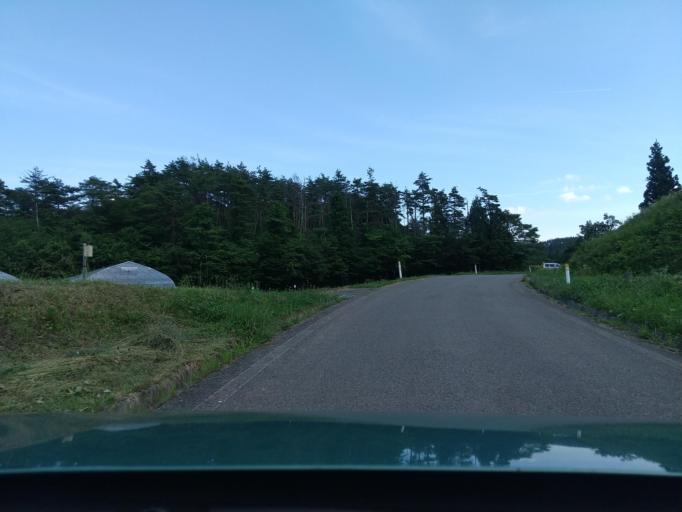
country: JP
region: Iwate
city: Ichinoseki
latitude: 39.0080
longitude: 141.2248
